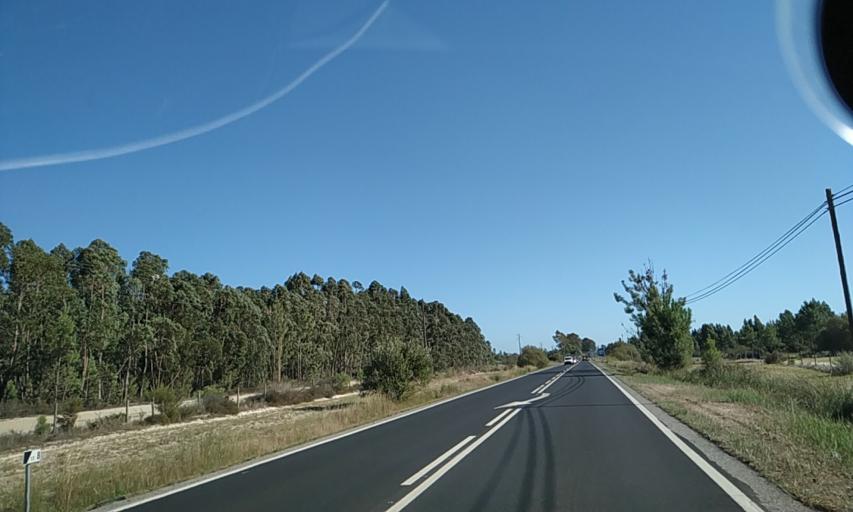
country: PT
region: Setubal
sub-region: Alcochete
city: Alcochete
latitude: 38.7965
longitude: -8.8808
